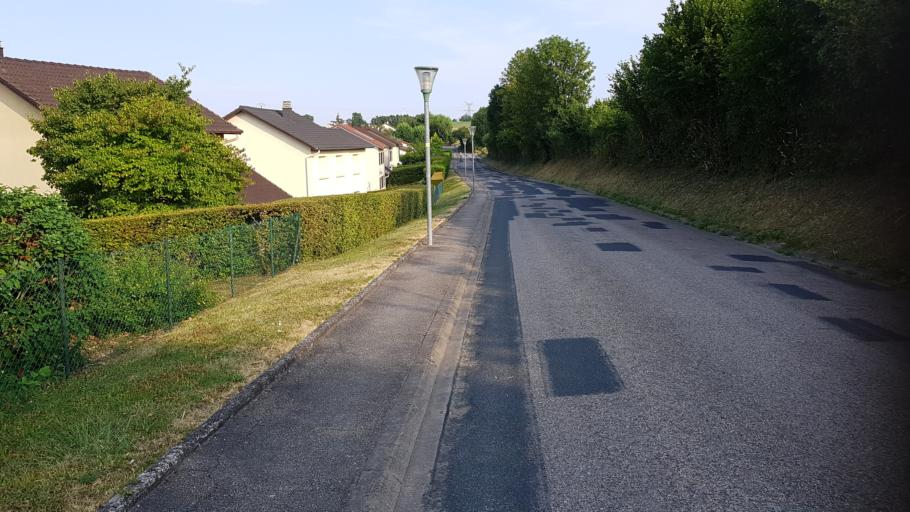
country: FR
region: Lorraine
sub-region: Departement des Vosges
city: Vittel
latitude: 48.1944
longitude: 5.9584
